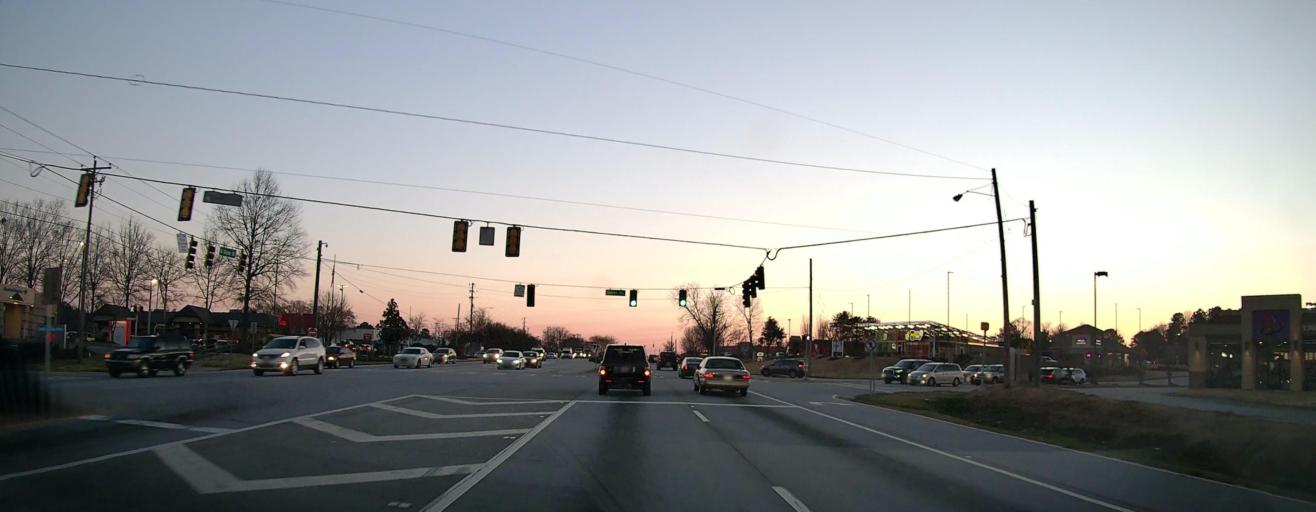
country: US
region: Georgia
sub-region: Fayette County
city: Fayetteville
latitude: 33.4687
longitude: -84.4467
